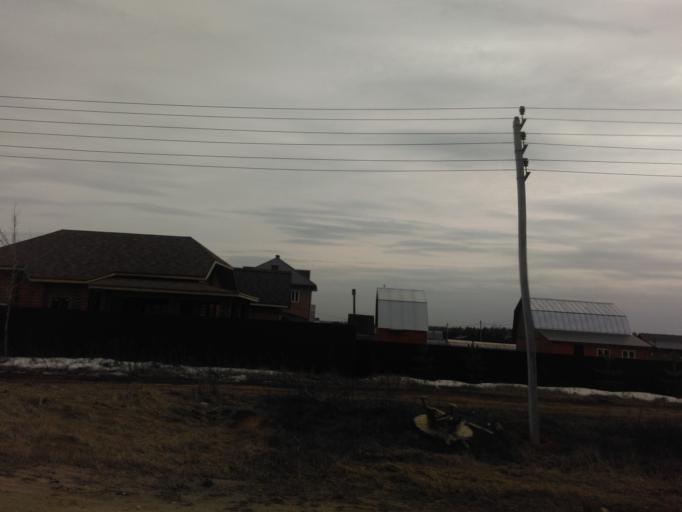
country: RU
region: Moskovskaya
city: Karinskoye
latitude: 55.7052
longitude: 36.6575
